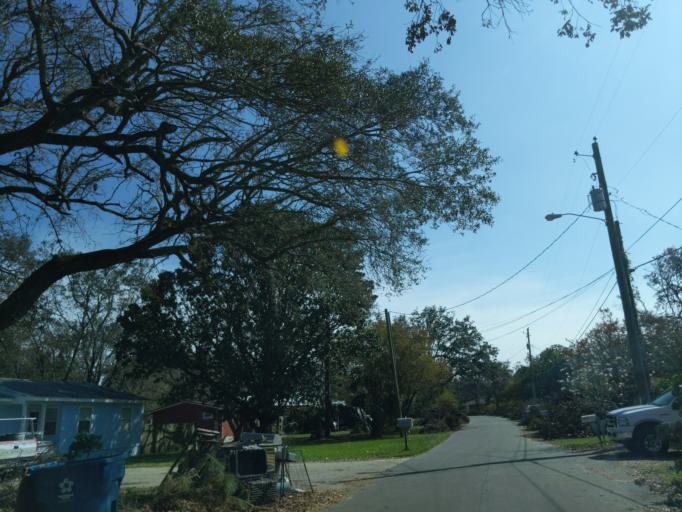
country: US
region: Florida
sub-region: Santa Rosa County
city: Gulf Breeze
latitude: 30.3589
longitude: -87.1927
